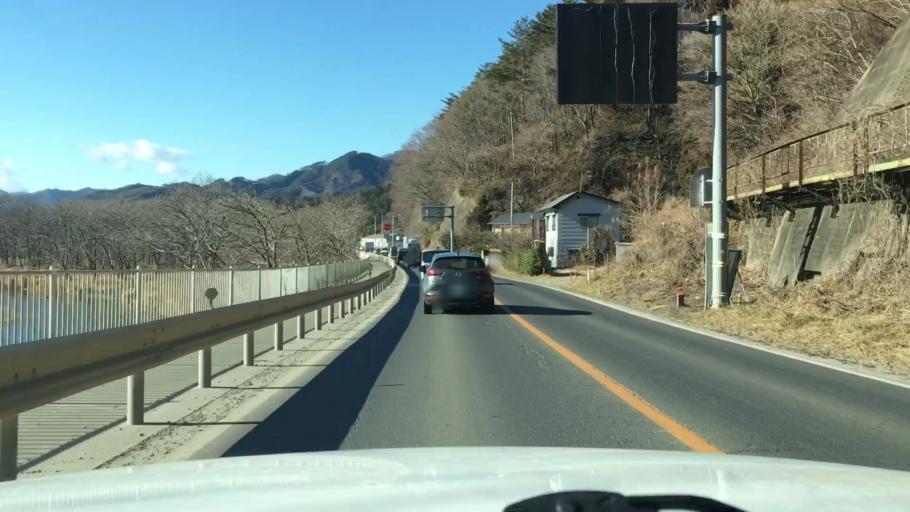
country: JP
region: Iwate
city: Miyako
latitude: 39.6316
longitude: 141.9049
